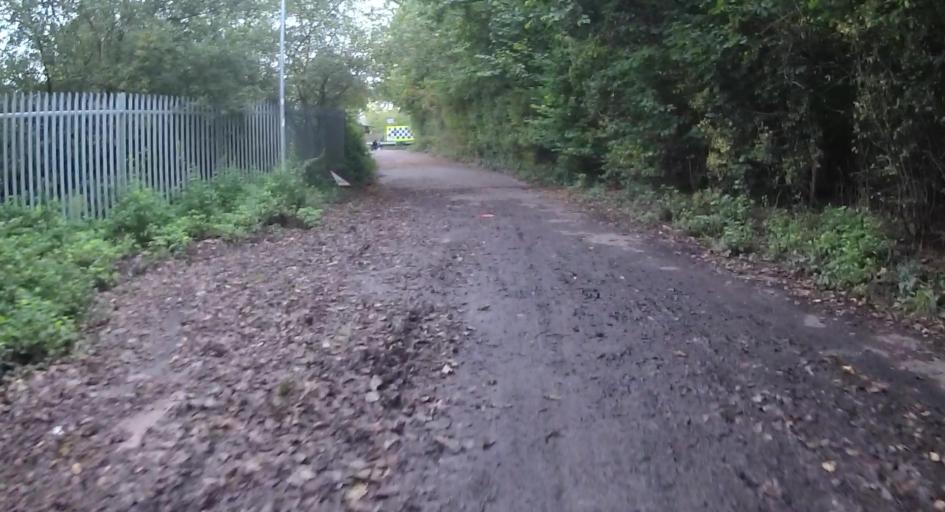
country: GB
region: England
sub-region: Bracknell Forest
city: Binfield
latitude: 51.4122
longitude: -0.7826
